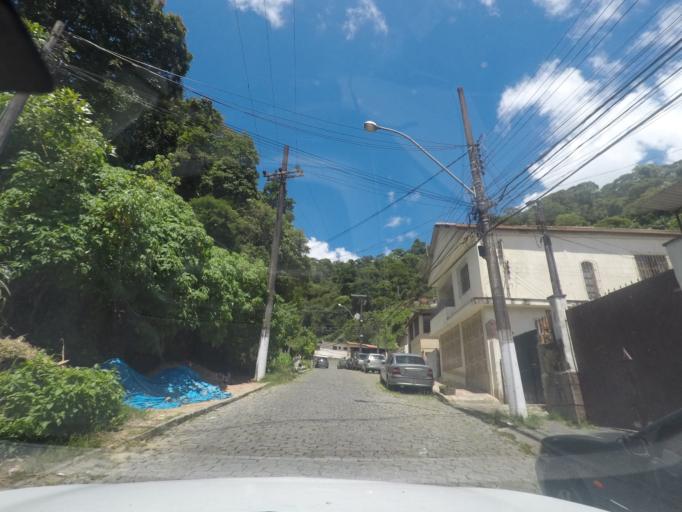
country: BR
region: Rio de Janeiro
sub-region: Teresopolis
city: Teresopolis
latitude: -22.4228
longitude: -42.9865
